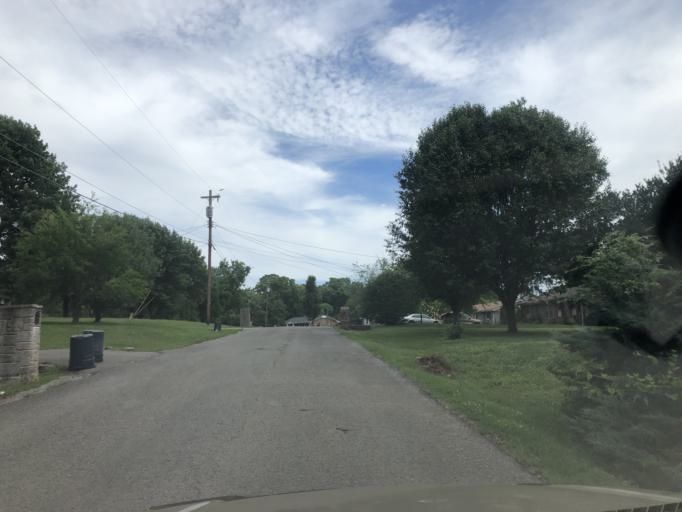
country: US
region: Tennessee
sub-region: Davidson County
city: Lakewood
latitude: 36.2602
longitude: -86.6117
